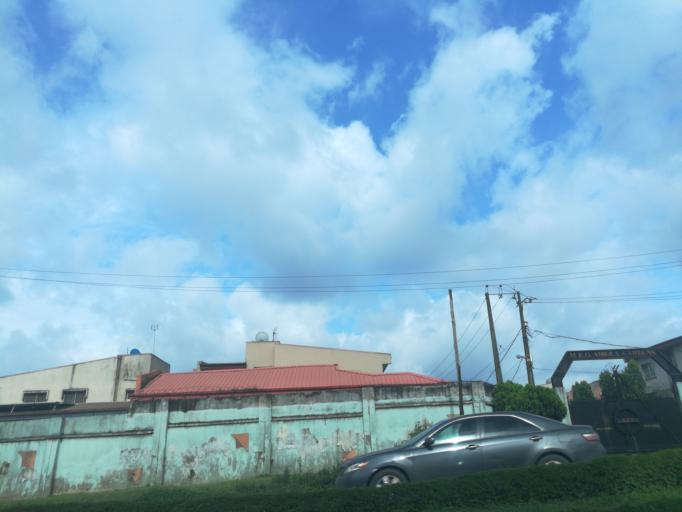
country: NG
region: Lagos
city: Ikeja
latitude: 6.6223
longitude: 3.3579
